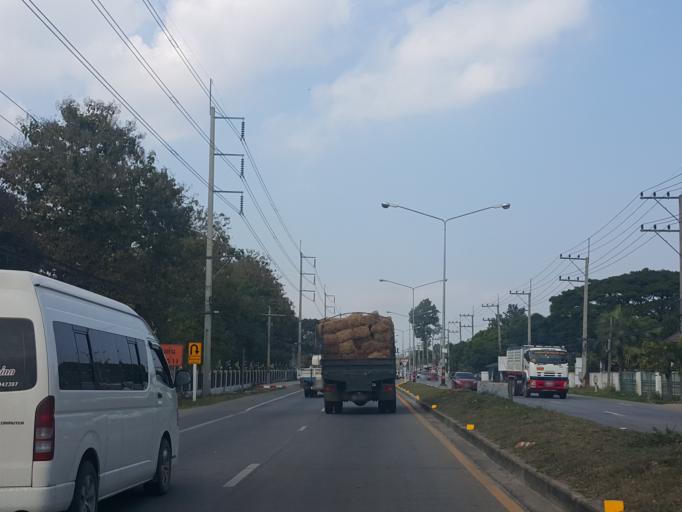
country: TH
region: Chiang Mai
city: Chiang Mai
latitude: 18.8578
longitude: 98.9671
